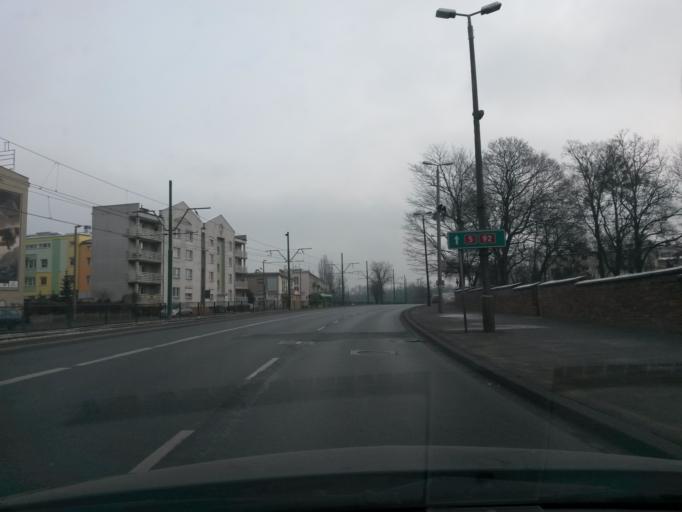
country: PL
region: Greater Poland Voivodeship
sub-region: Poznan
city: Poznan
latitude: 52.4097
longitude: 16.9585
